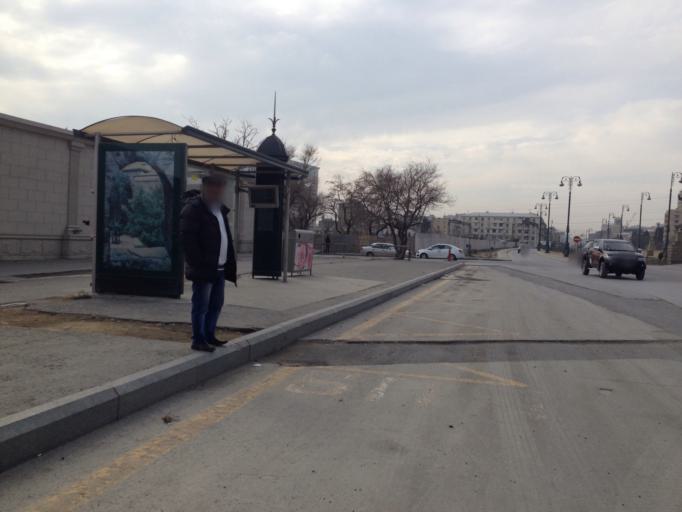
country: AZ
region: Baki
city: Baku
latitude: 40.4040
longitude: 49.8847
